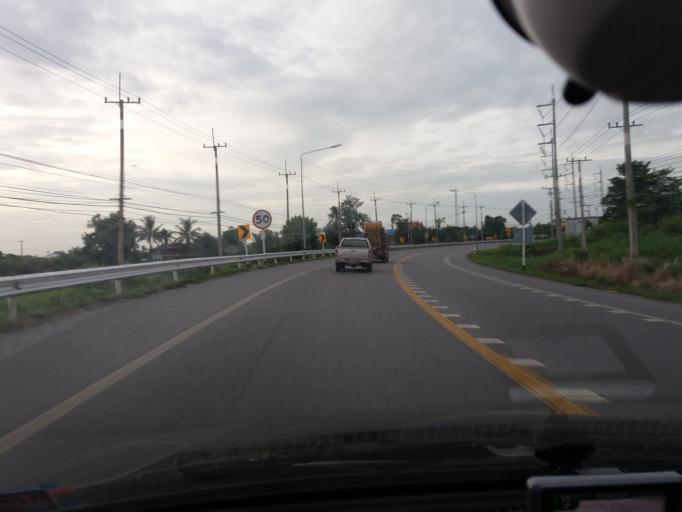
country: TH
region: Suphan Buri
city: U Thong
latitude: 14.4781
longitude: 99.9376
